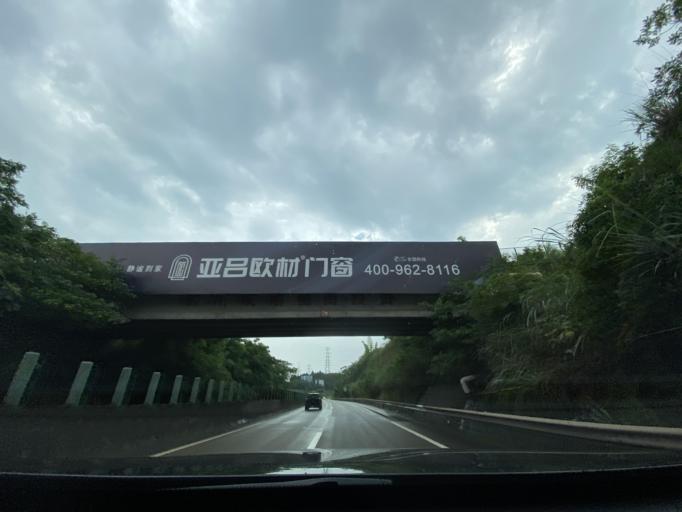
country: CN
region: Sichuan
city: Yanjiang
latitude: 30.0846
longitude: 104.5983
